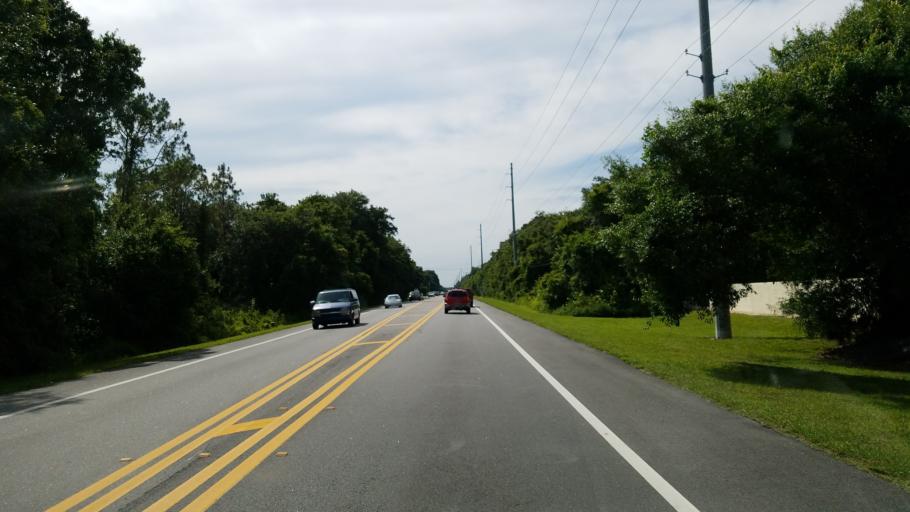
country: US
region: Florida
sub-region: Hillsborough County
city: Fish Hawk
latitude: 27.8522
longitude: -82.1843
